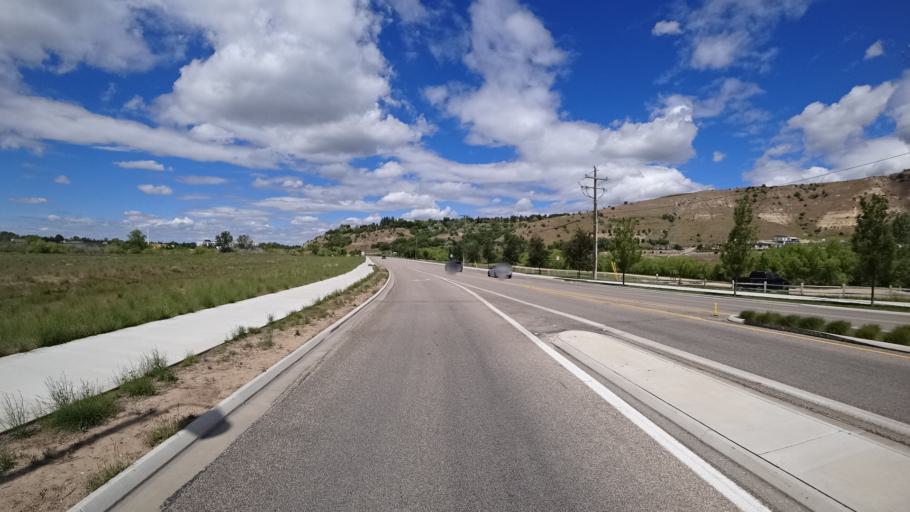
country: US
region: Idaho
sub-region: Ada County
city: Boise
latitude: 43.5766
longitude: -116.1403
